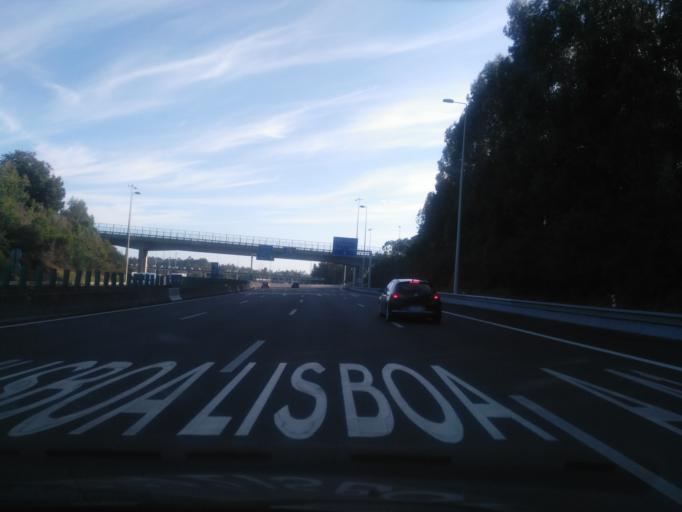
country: PT
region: Porto
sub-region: Vila Nova de Gaia
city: Grijo
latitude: 41.0205
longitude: -8.5804
